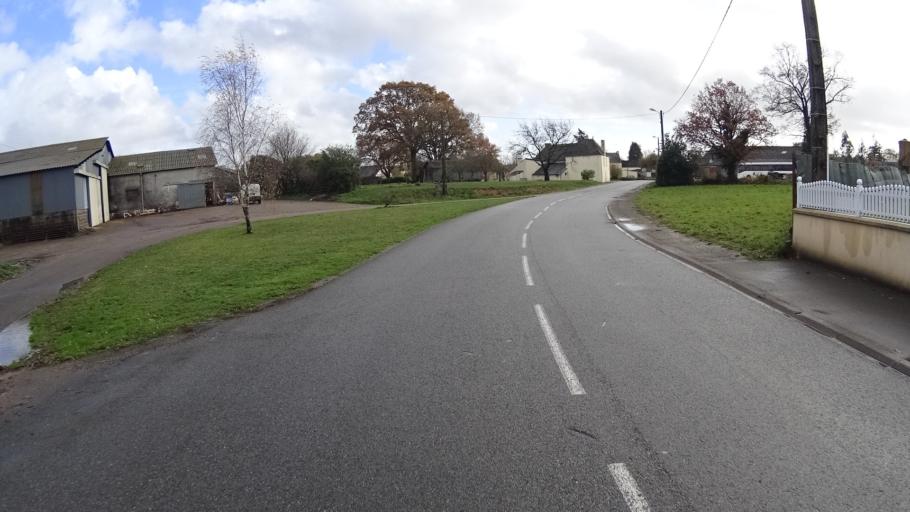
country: FR
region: Brittany
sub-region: Departement du Morbihan
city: Rieux
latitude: 47.5699
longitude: -2.1167
